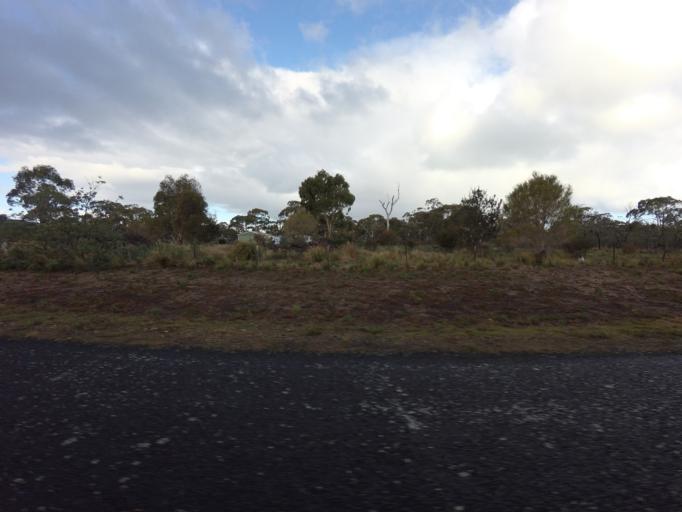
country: AU
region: Tasmania
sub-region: Break O'Day
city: St Helens
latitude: -42.1027
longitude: 148.0730
